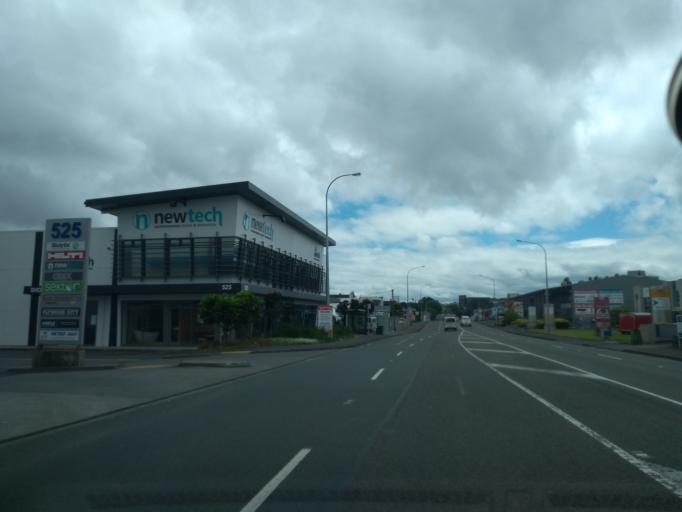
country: NZ
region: Auckland
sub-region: Auckland
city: Tamaki
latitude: -36.9072
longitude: 174.8117
